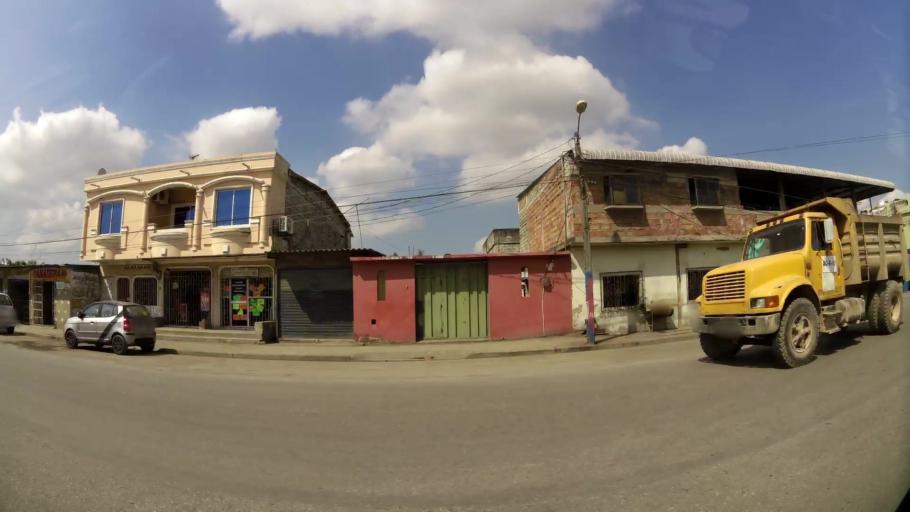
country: EC
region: Guayas
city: Eloy Alfaro
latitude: -2.1530
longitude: -79.8270
